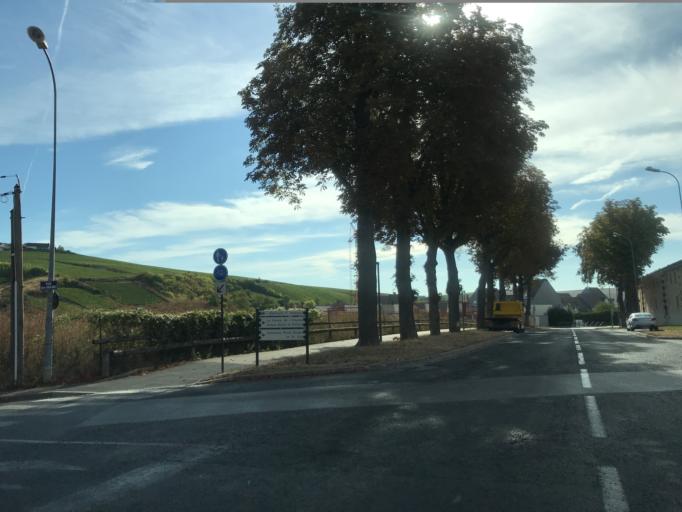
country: FR
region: Champagne-Ardenne
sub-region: Departement de la Marne
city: Pierry
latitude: 49.0289
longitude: 3.9557
